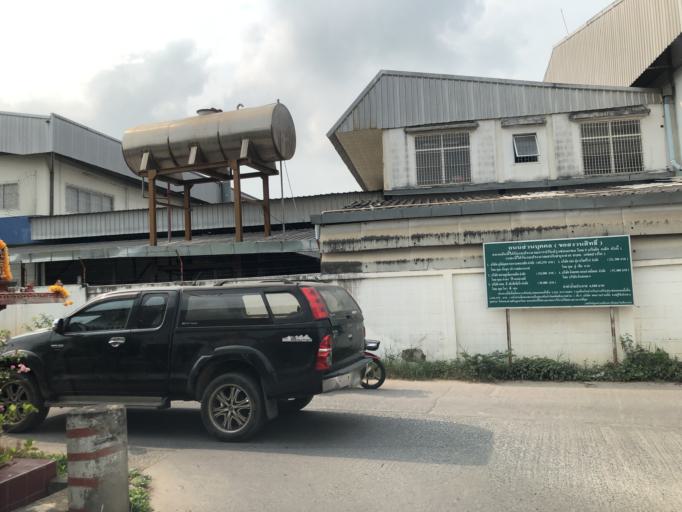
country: TH
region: Samut Prakan
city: Bang Bo District
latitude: 13.5827
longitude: 100.7129
